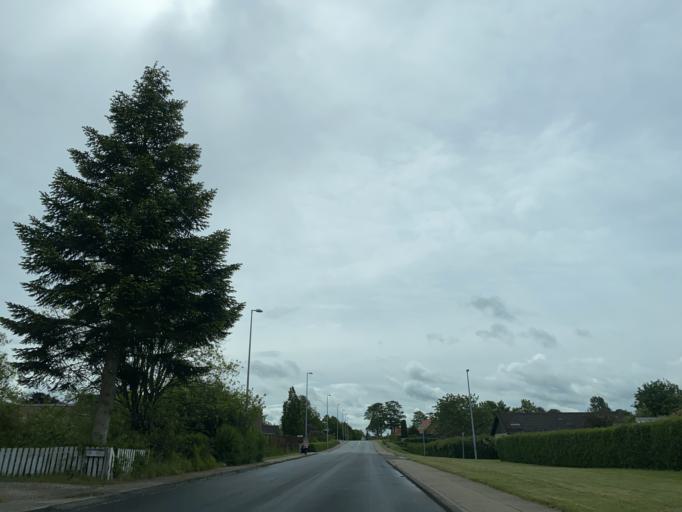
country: DK
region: Central Jutland
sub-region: Favrskov Kommune
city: Hammel
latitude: 56.2533
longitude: 9.8715
